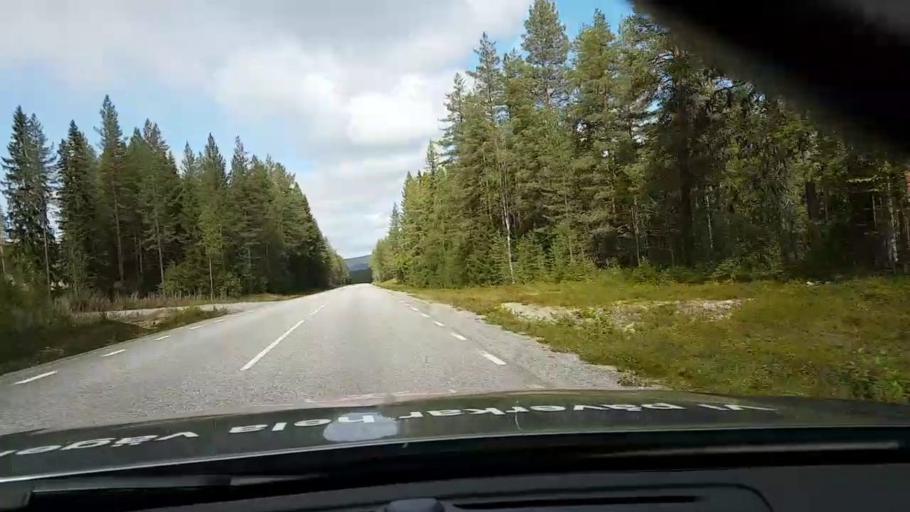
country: SE
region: Vaesternorrland
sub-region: OErnskoeldsviks Kommun
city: Bredbyn
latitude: 63.6967
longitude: 17.7643
